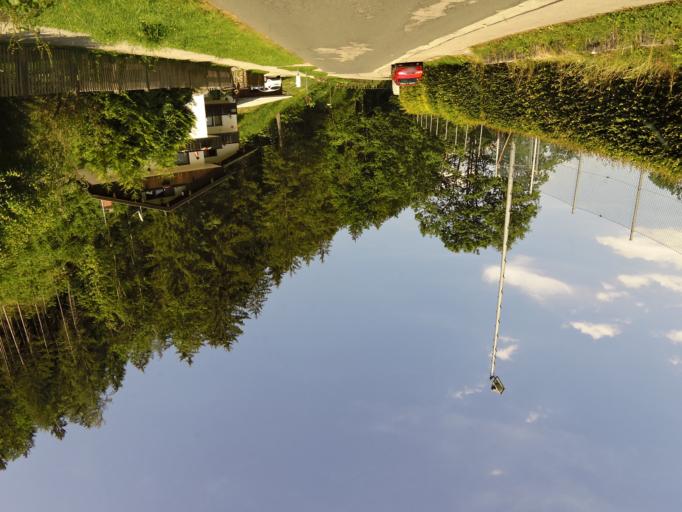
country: DE
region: Bavaria
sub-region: Upper Bavaria
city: Berchtesgaden
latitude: 47.6360
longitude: 13.0137
